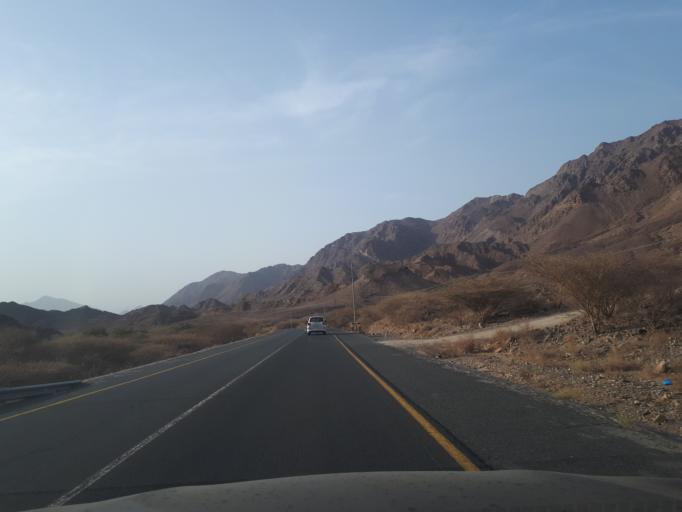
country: OM
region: Muhafazat ad Dakhiliyah
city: Sufalat Sama'il
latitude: 23.1662
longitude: 58.1028
